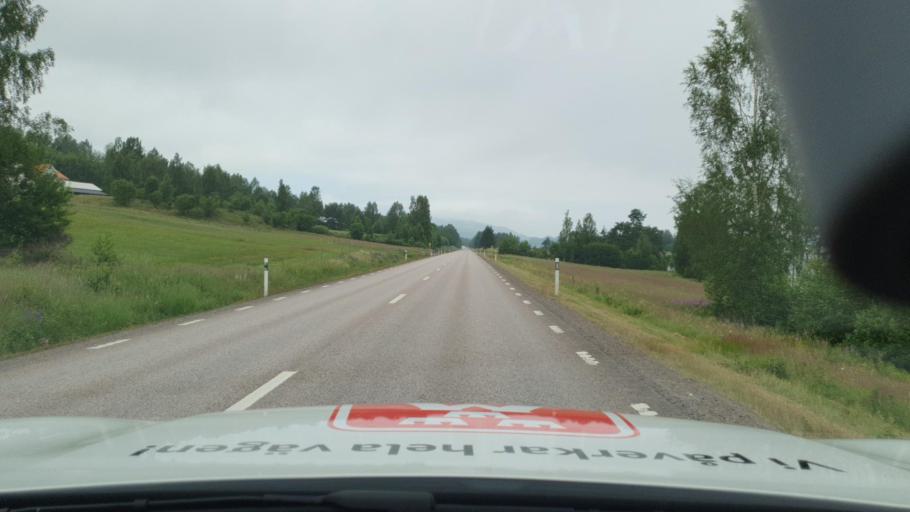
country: SE
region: Vaermland
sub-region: Sunne Kommun
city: Sunne
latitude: 59.9293
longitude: 13.1272
